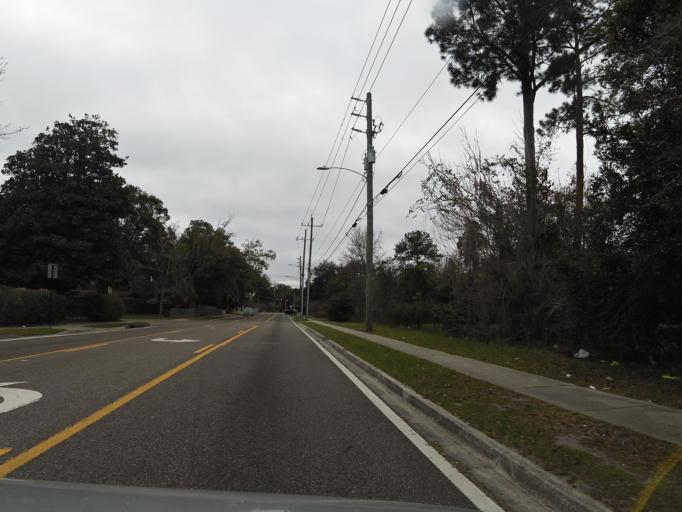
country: US
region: Florida
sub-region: Duval County
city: Jacksonville
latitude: 30.3764
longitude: -81.7151
